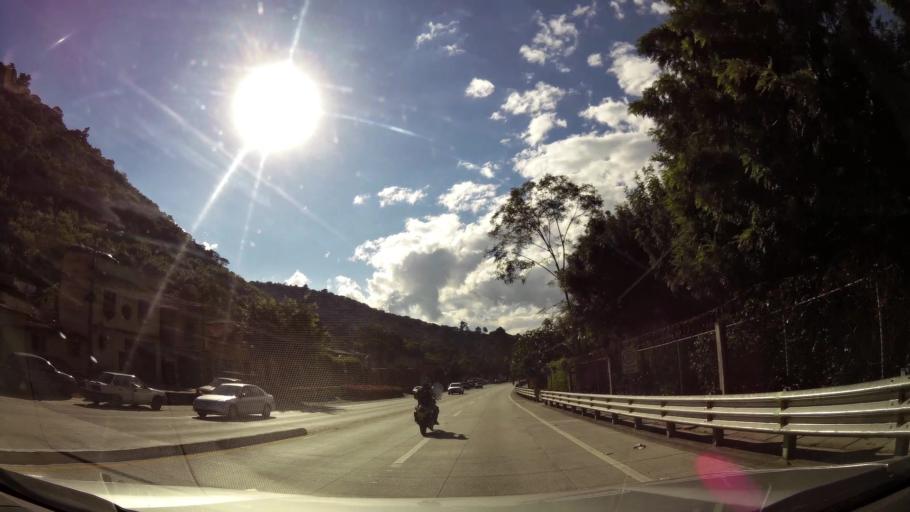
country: GT
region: Sacatepequez
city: Antigua Guatemala
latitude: 14.5584
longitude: -90.7151
